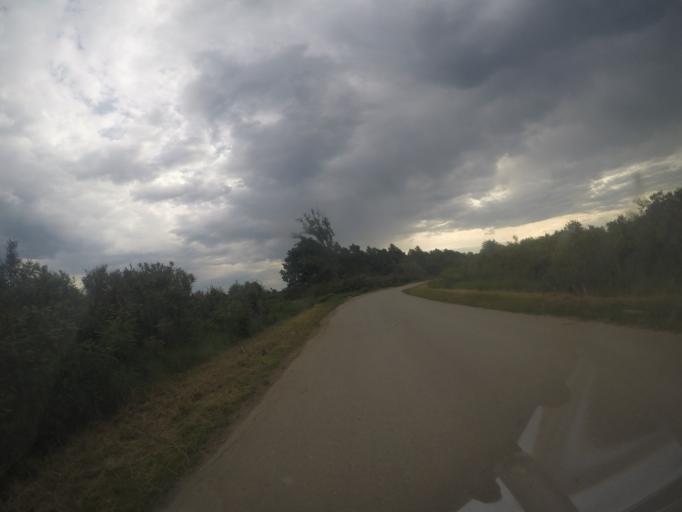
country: RS
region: Central Serbia
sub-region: Belgrade
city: Zemun
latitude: 44.8984
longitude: 20.4029
